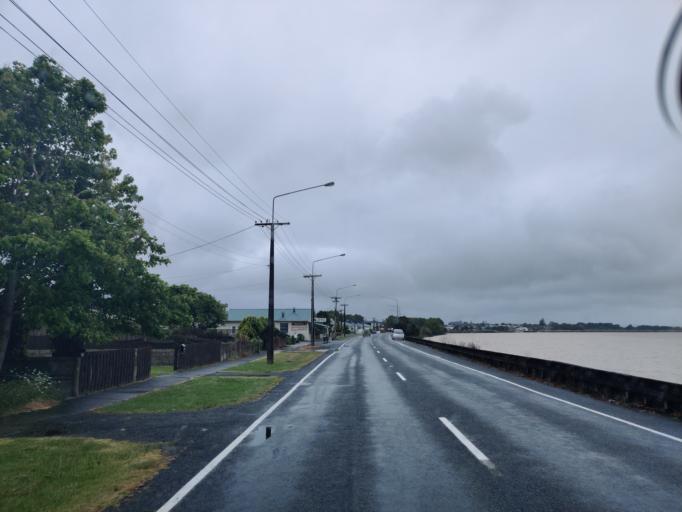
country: NZ
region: Northland
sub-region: Kaipara District
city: Dargaville
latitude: -35.9491
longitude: 173.8653
